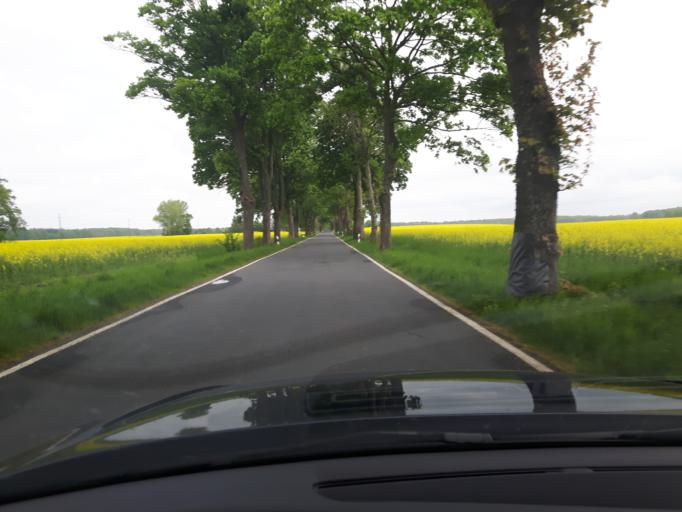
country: DE
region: Mecklenburg-Vorpommern
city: Velgast
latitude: 54.2082
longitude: 12.7321
